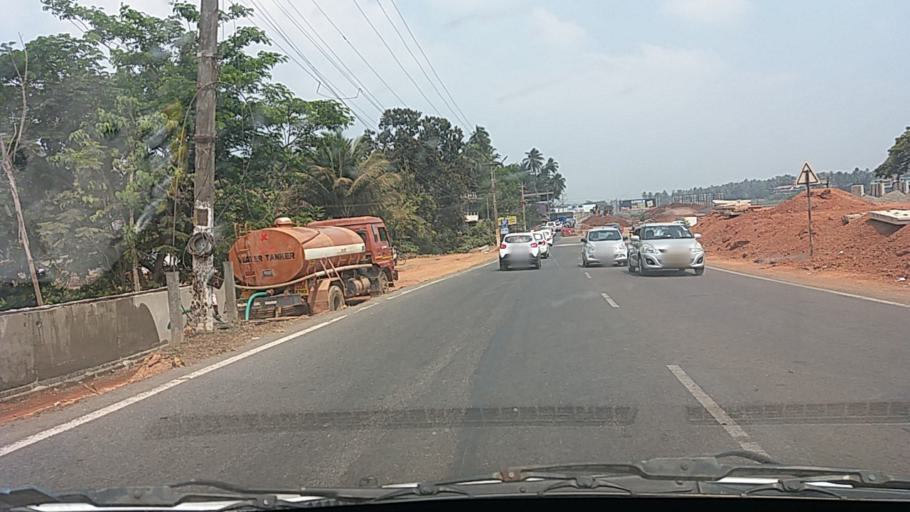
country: IN
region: Goa
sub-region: North Goa
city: Bambolim
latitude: 15.4709
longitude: 73.8504
